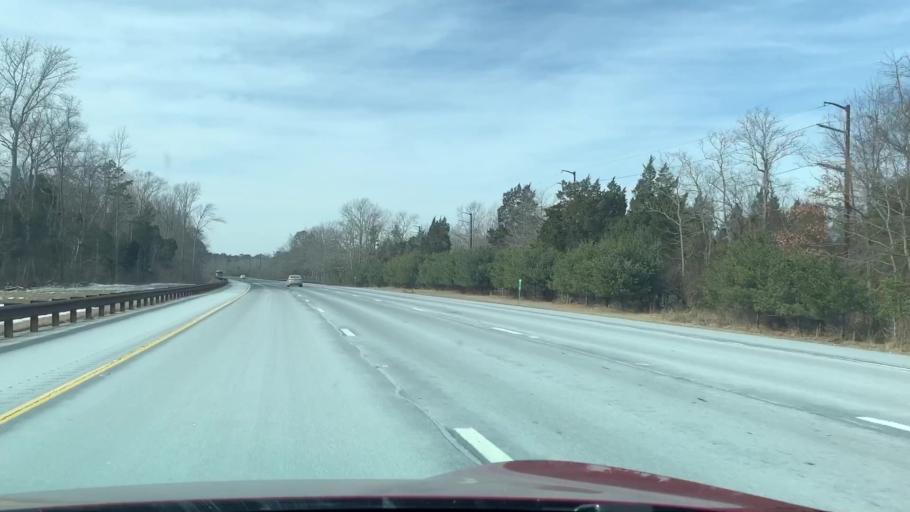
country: US
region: New Jersey
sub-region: Atlantic County
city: Port Republic
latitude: 39.5406
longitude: -74.4803
